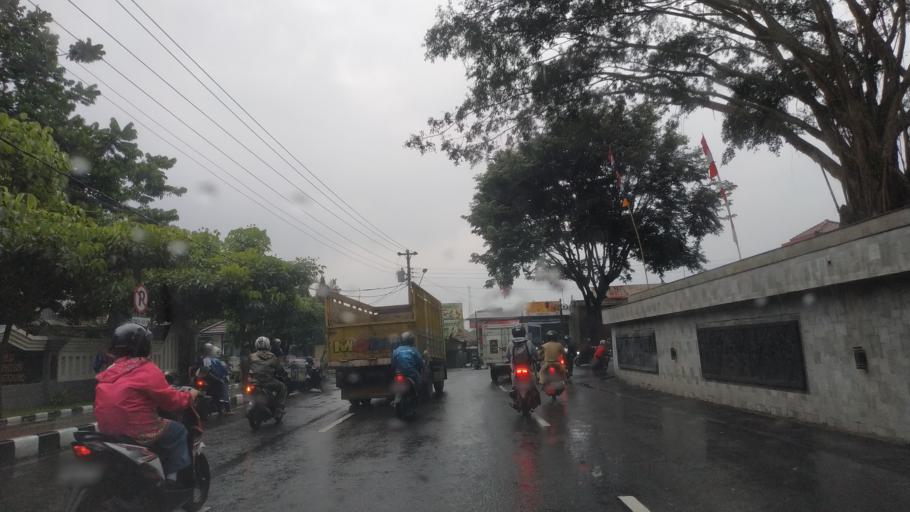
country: ID
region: Central Java
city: Magelang
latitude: -7.3165
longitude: 110.1760
